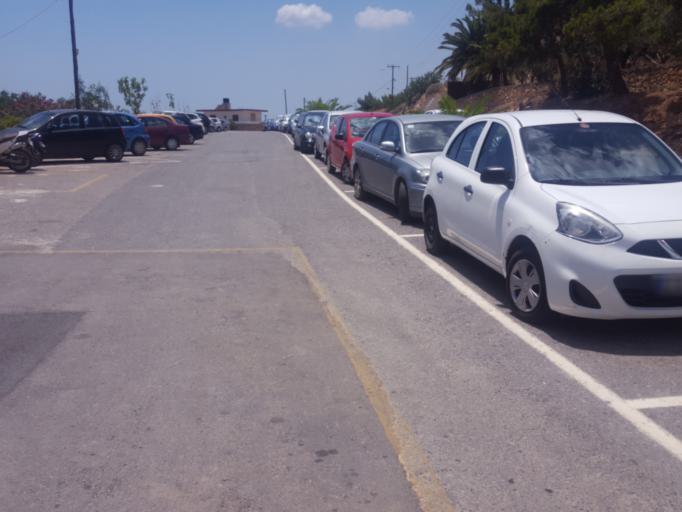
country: GR
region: Crete
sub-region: Nomos Lasithiou
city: Kato Chorio
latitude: 35.0130
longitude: 25.8403
